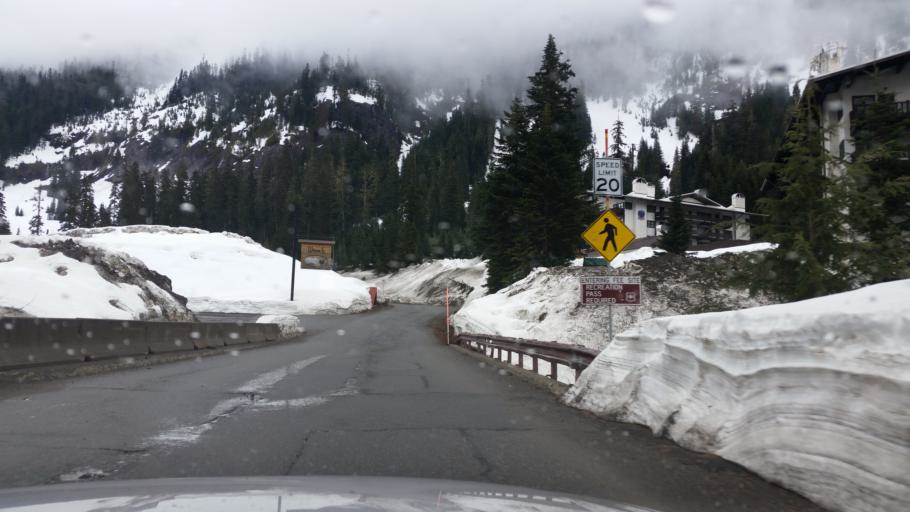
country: US
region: Washington
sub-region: King County
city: Tanner
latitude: 47.4429
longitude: -121.4232
